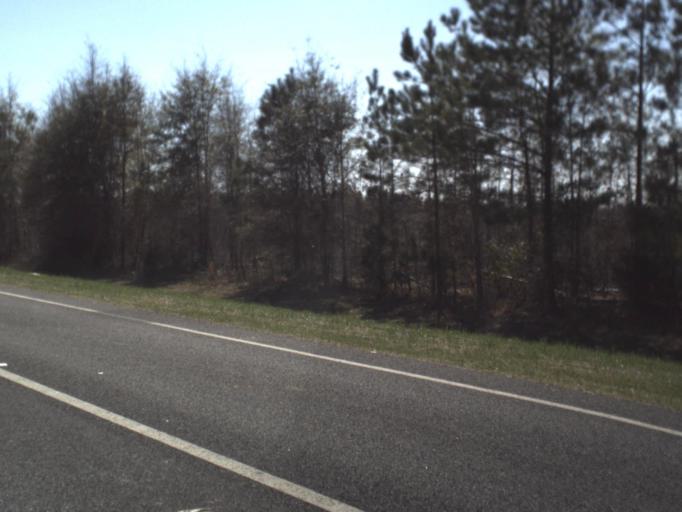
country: US
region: Florida
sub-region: Jackson County
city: Graceville
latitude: 30.8863
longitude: -85.3673
